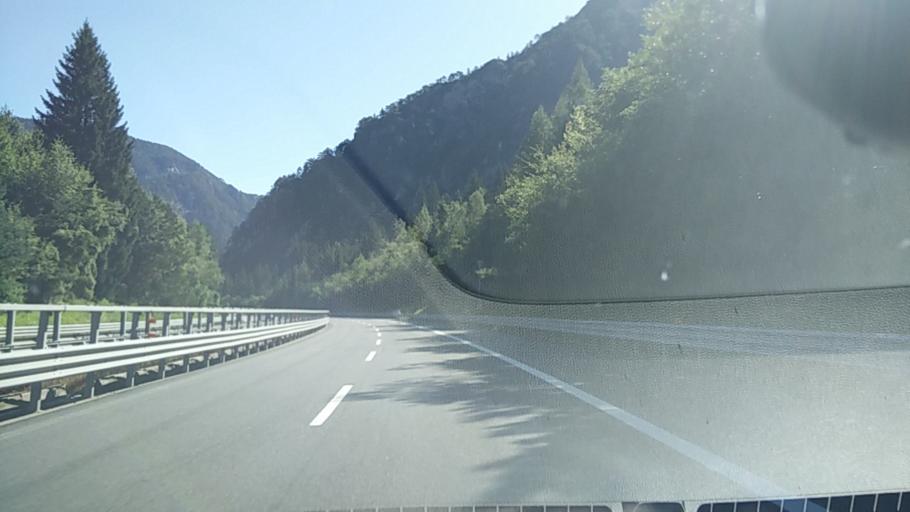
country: IT
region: Friuli Venezia Giulia
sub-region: Provincia di Udine
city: Malborghetto
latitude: 46.5047
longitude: 13.4541
